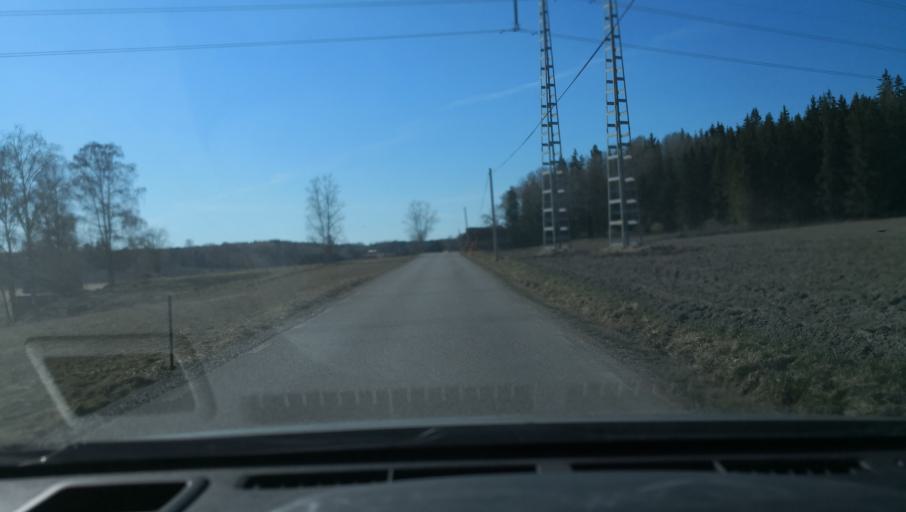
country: SE
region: Vaestmanland
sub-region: Sala Kommun
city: Sala
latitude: 60.0772
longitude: 16.4764
